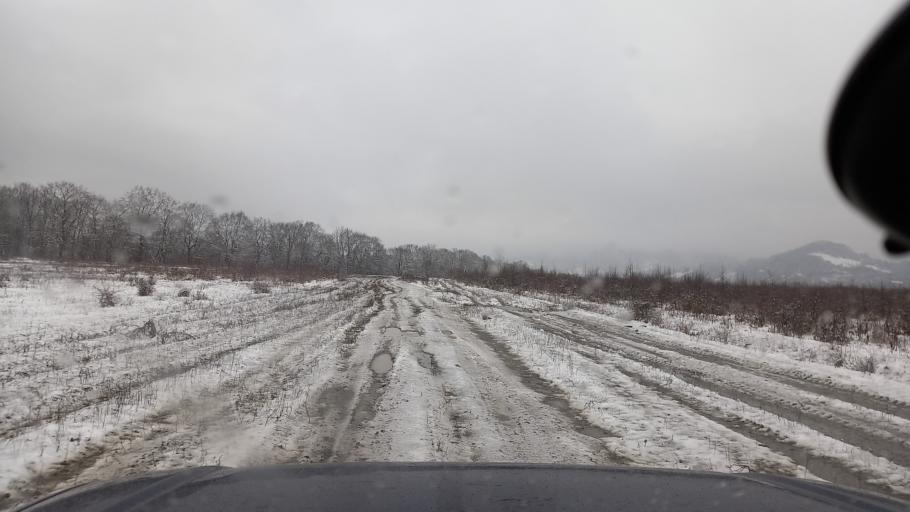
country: RU
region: Adygeya
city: Kamennomostskiy
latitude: 44.2196
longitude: 40.1787
